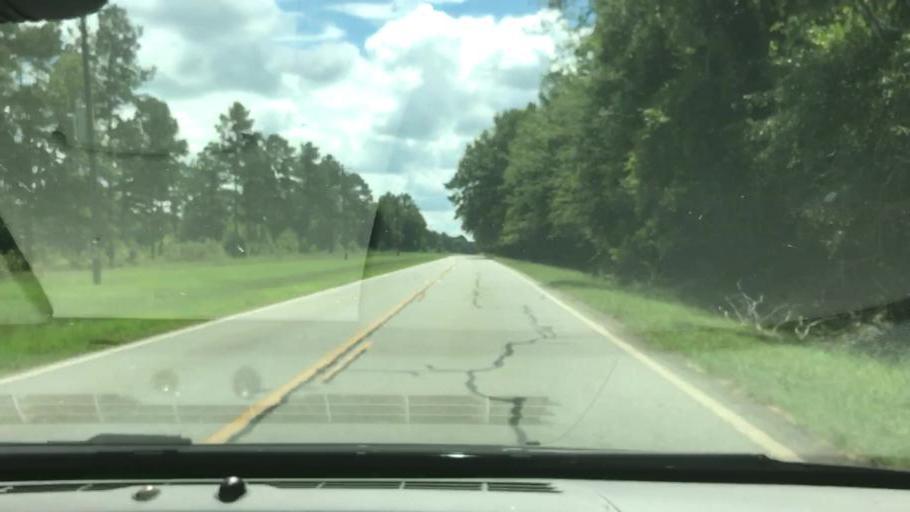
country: US
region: Georgia
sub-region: Quitman County
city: Georgetown
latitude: 32.1115
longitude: -85.0380
